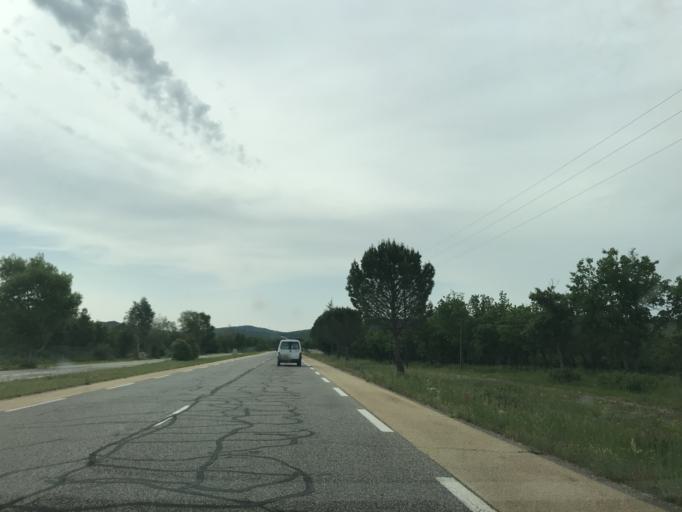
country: FR
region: Provence-Alpes-Cote d'Azur
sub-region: Departement du Var
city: Rians
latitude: 43.5627
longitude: 5.7843
